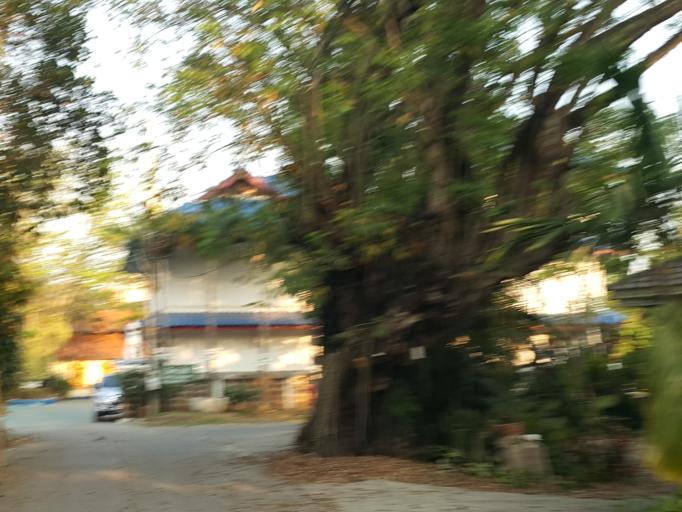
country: TH
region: Chiang Mai
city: San Sai
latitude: 18.8999
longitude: 98.9431
